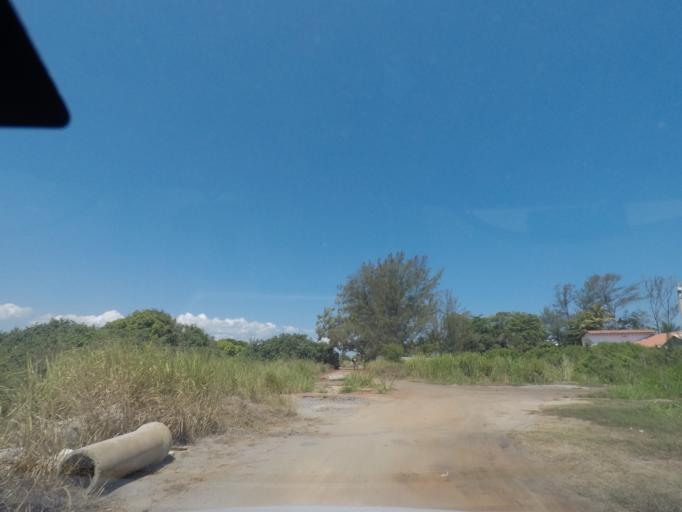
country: BR
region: Rio de Janeiro
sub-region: Marica
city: Marica
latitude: -22.9724
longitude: -42.9192
